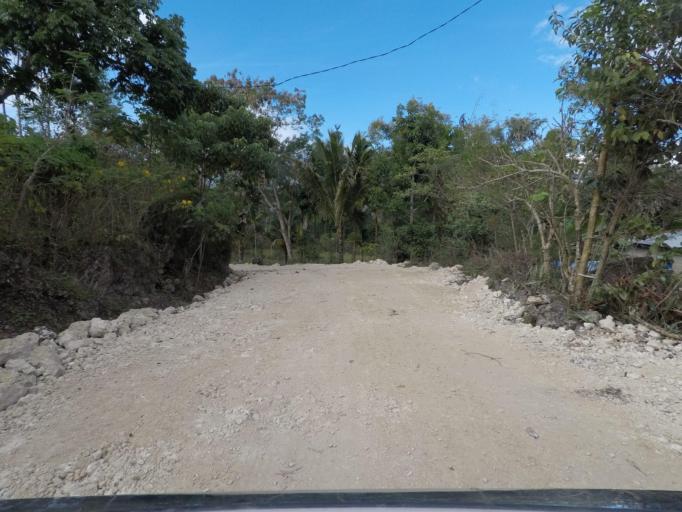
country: TL
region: Baucau
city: Venilale
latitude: -8.6457
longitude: 126.3915
